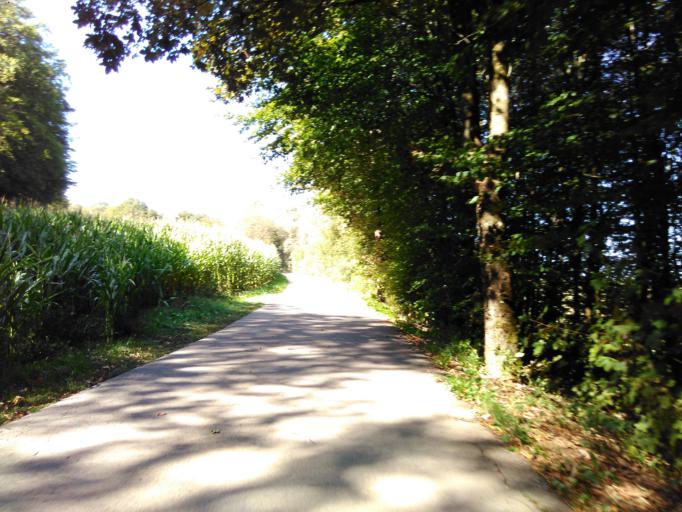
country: LU
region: Diekirch
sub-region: Canton de Redange
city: Rambrouch
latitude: 49.8142
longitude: 5.8383
